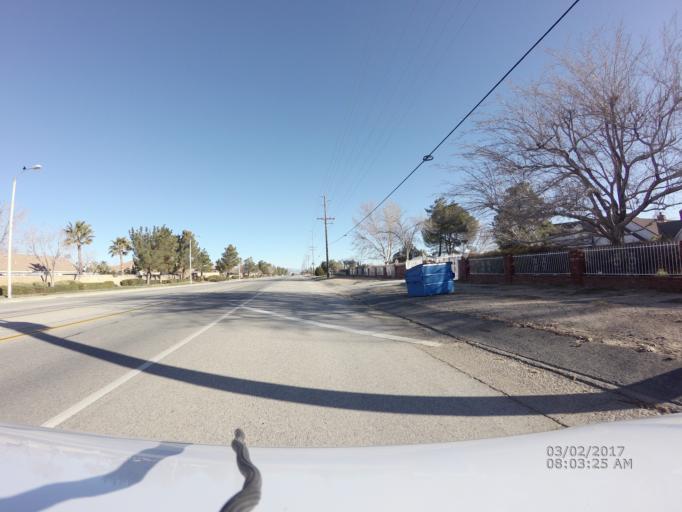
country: US
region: California
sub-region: Los Angeles County
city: Desert View Highlands
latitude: 34.6177
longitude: -118.1836
